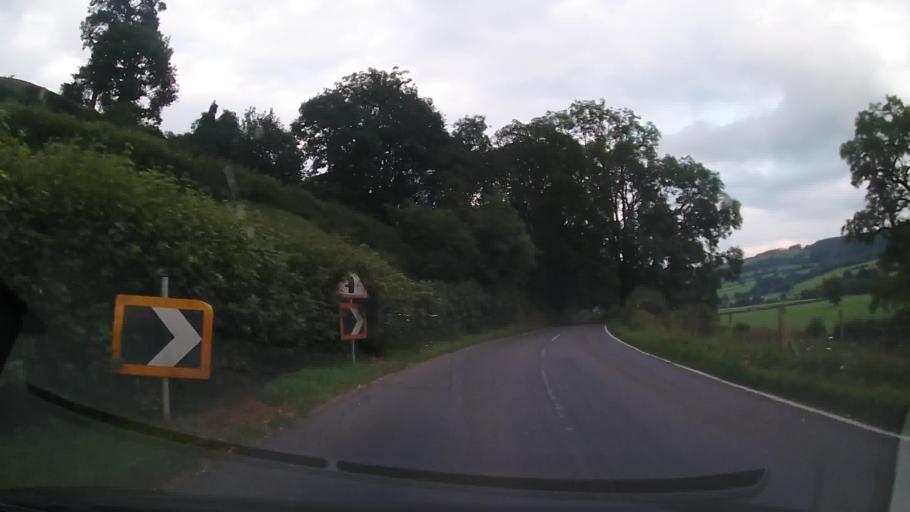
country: GB
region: Wales
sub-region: Sir Powys
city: Llanfechain
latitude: 52.8120
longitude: -3.2353
